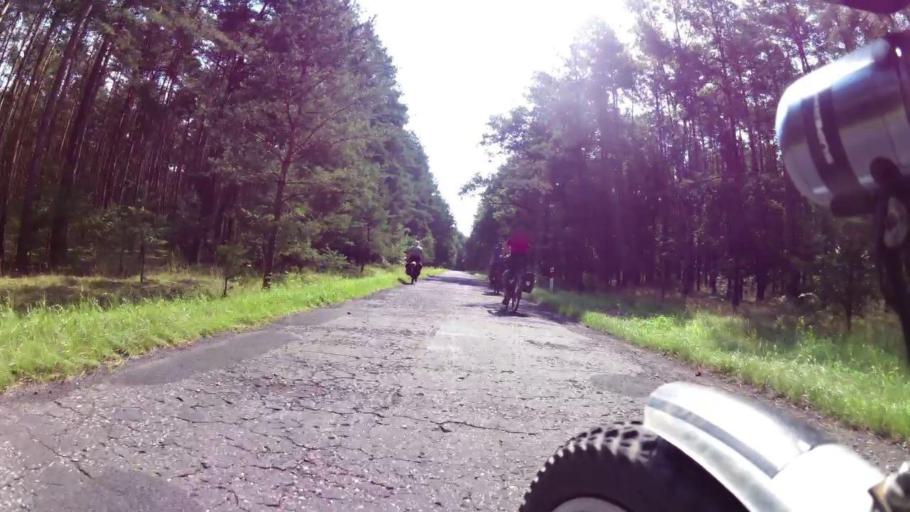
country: PL
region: West Pomeranian Voivodeship
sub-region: Powiat mysliborski
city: Boleszkowice
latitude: 52.6748
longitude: 14.5153
